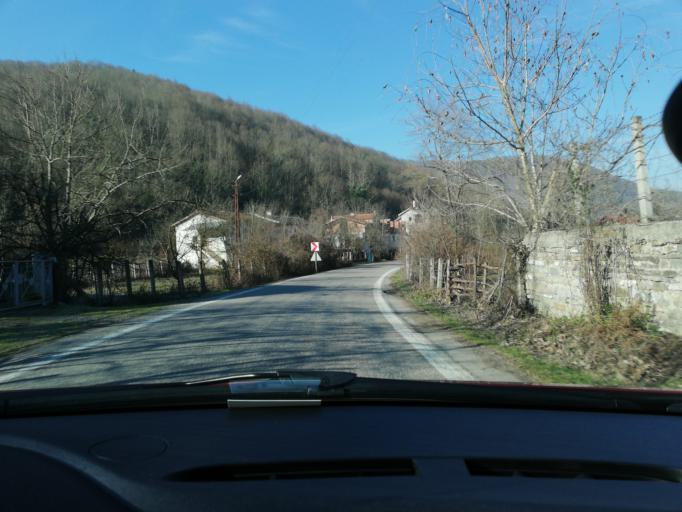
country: TR
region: Bartin
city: Kumluca
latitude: 41.4539
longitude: 32.5311
